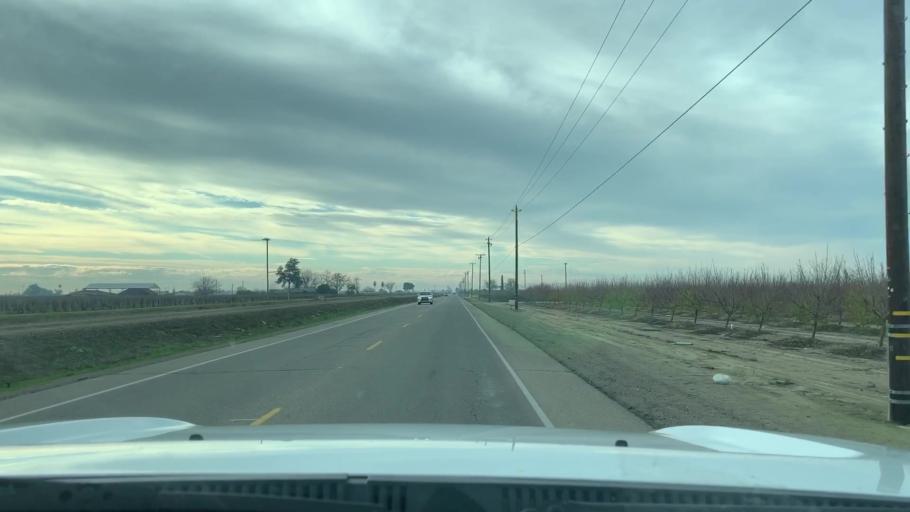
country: US
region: California
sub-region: Fresno County
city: Fowler
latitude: 36.6055
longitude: -119.7057
